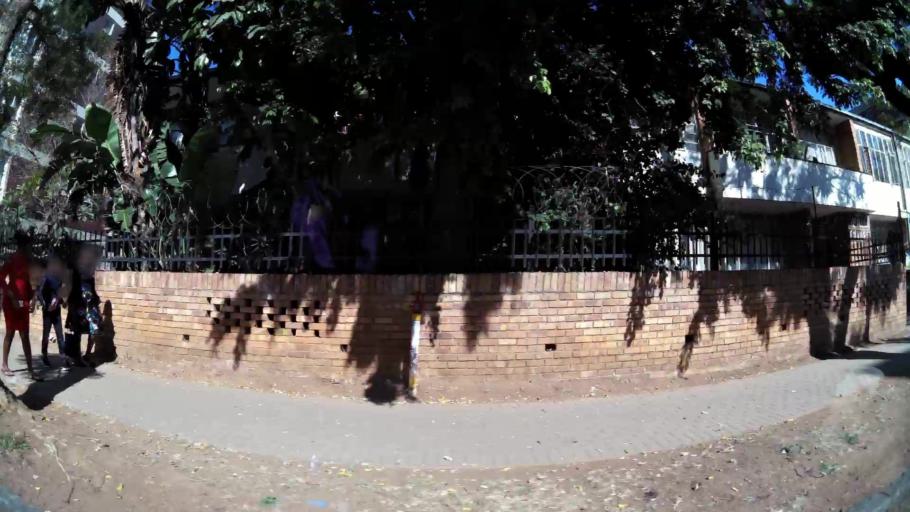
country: ZA
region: Gauteng
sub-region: City of Tshwane Metropolitan Municipality
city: Pretoria
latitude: -25.7570
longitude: 28.2110
